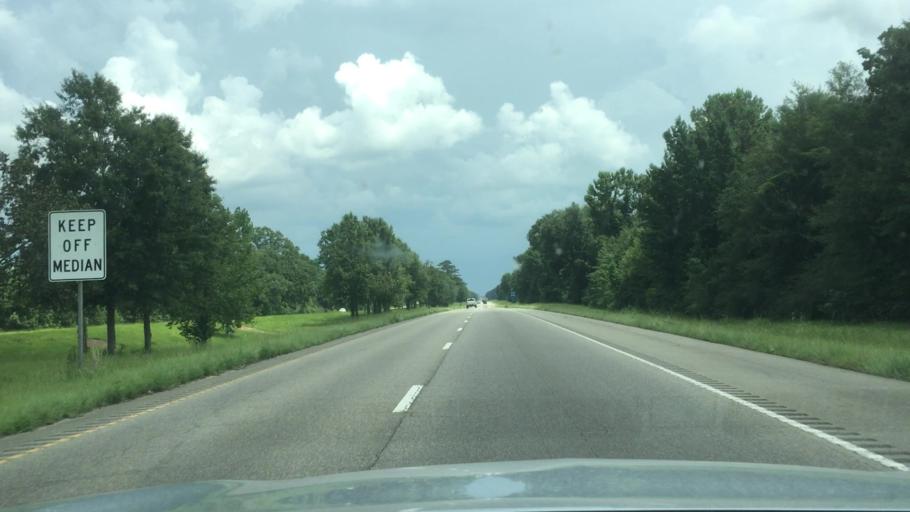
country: US
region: Mississippi
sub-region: Pearl River County
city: Picayune
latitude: 30.5526
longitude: -89.6442
